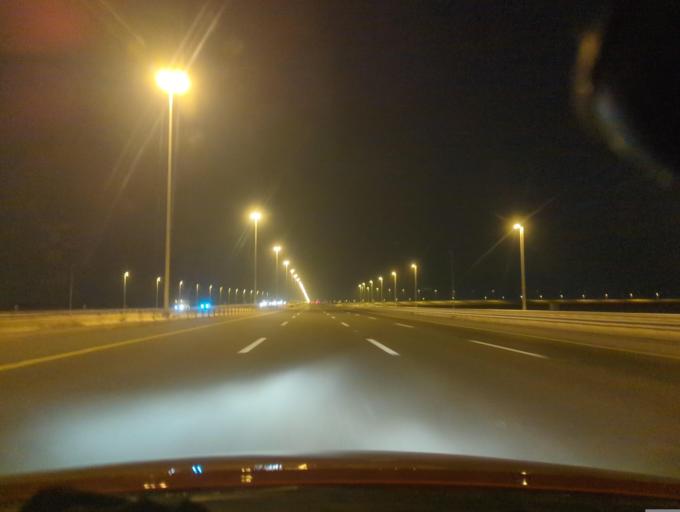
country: AE
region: Abu Dhabi
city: Abu Dhabi
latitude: 24.4622
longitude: 54.7496
